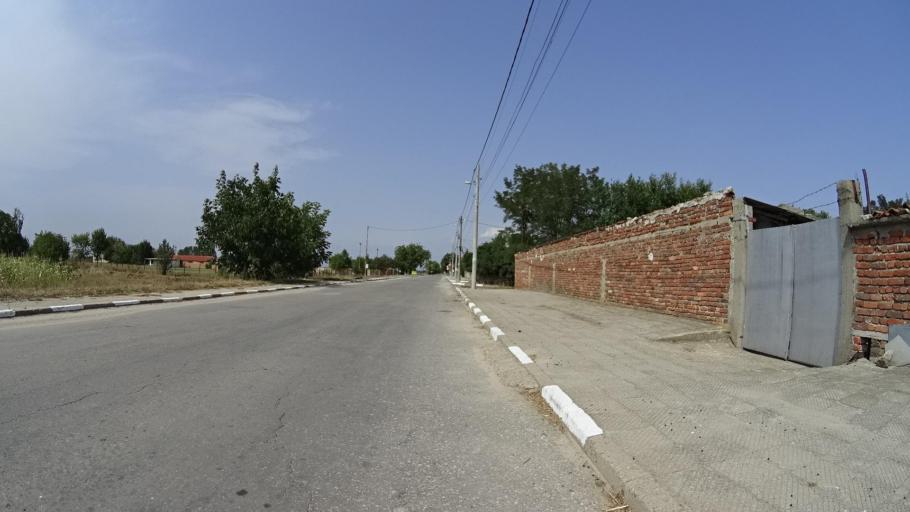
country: BG
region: Plovdiv
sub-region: Obshtina Plovdiv
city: Plovdiv
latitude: 42.2441
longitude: 24.7952
